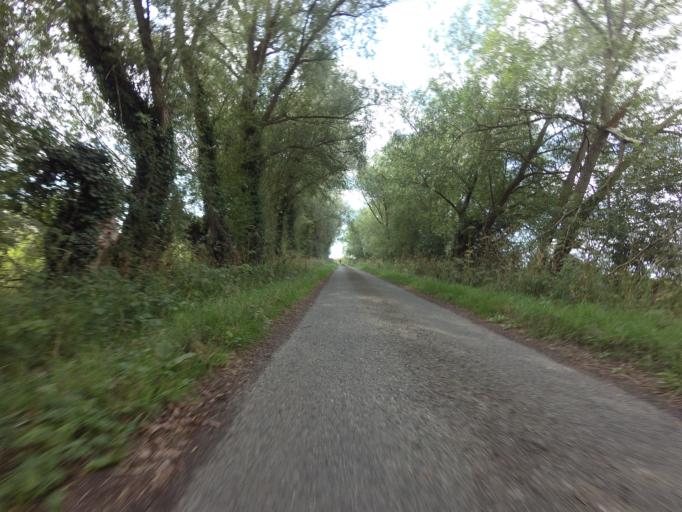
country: GB
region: England
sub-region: Kent
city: Stone
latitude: 51.0541
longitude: 0.7687
